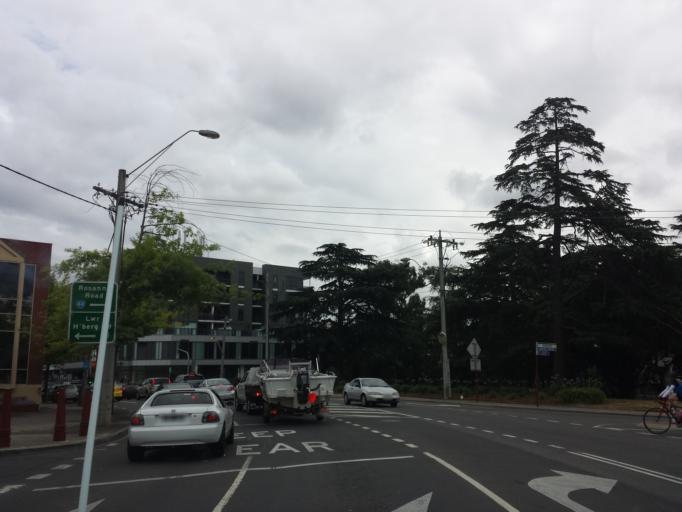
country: AU
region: Victoria
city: Rosanna
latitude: -37.7569
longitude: 145.0705
